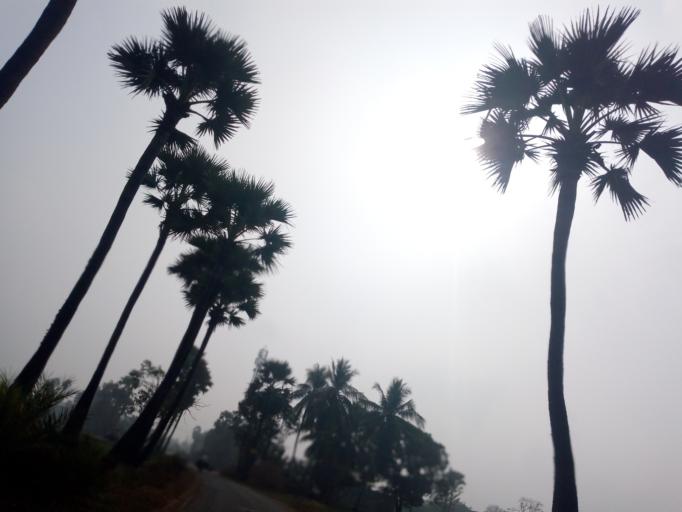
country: IN
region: Andhra Pradesh
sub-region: West Godavari
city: Tadepallegudem
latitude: 16.8392
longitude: 81.3429
